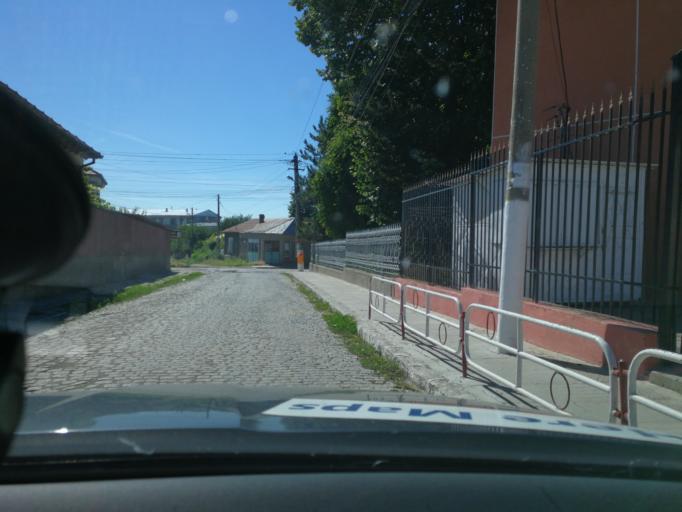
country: RO
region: Tulcea
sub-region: Oras Macin
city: Macin
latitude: 45.2436
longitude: 28.1310
